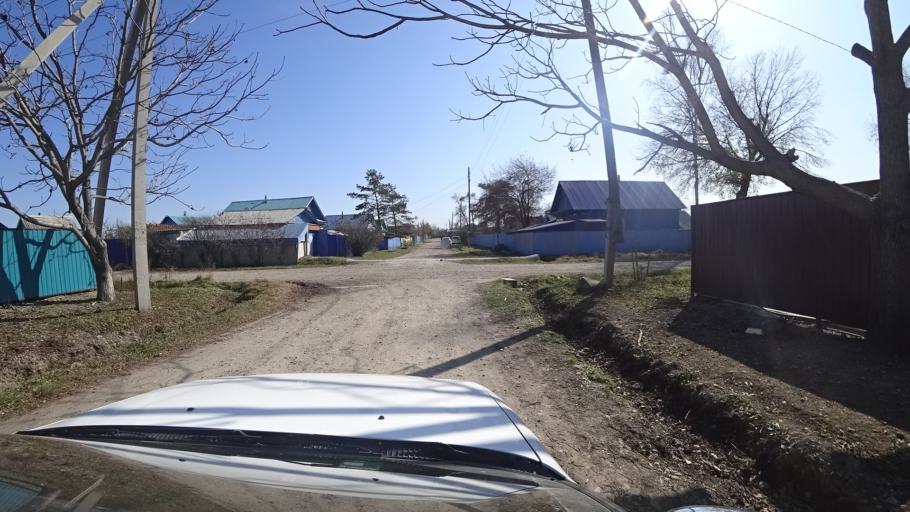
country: RU
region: Primorskiy
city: Dal'nerechensk
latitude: 45.9280
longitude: 133.7493
